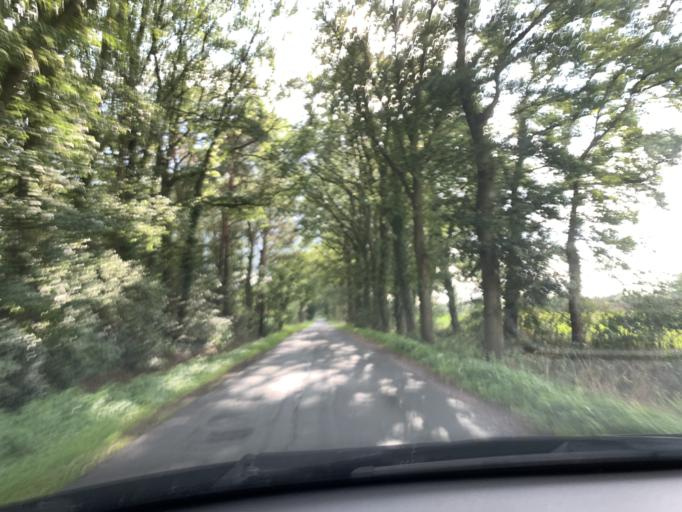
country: DE
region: Lower Saxony
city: Bockhorn
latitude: 53.3164
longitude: 7.9926
